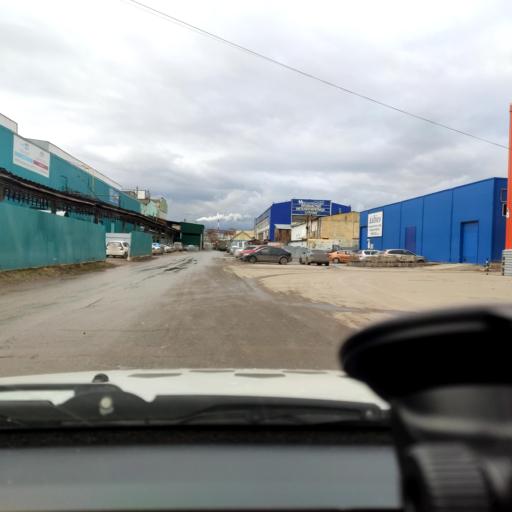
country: RU
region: Perm
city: Froly
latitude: 57.9609
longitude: 56.2776
